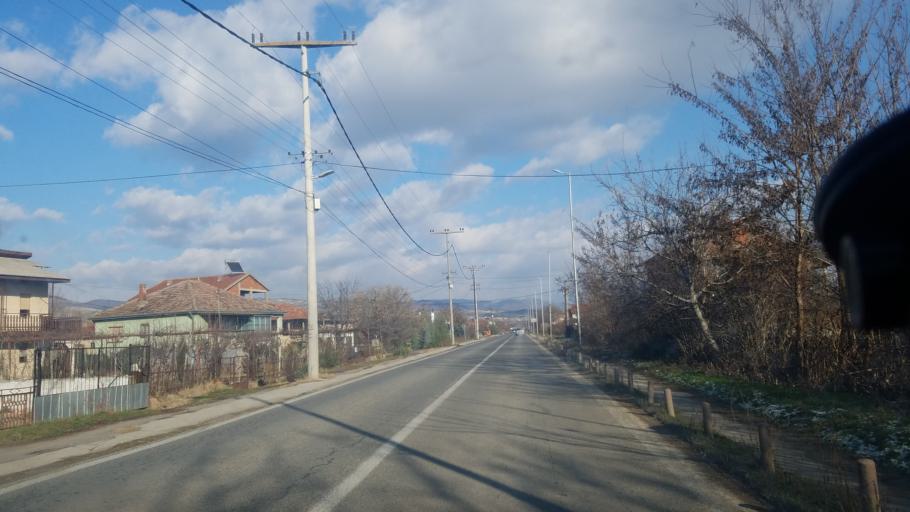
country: MK
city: Obleshevo
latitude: 41.8845
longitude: 22.3361
